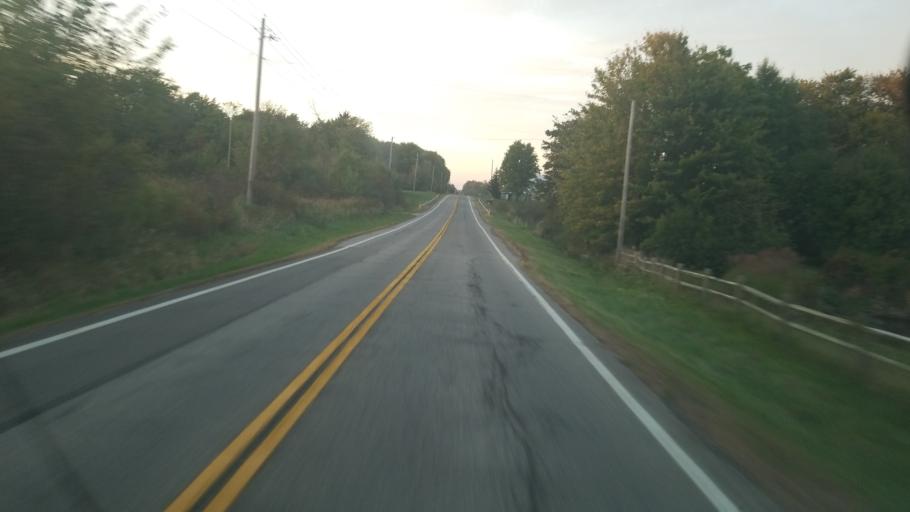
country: US
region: Ohio
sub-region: Ashtabula County
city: Andover
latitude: 41.6449
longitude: -80.6669
